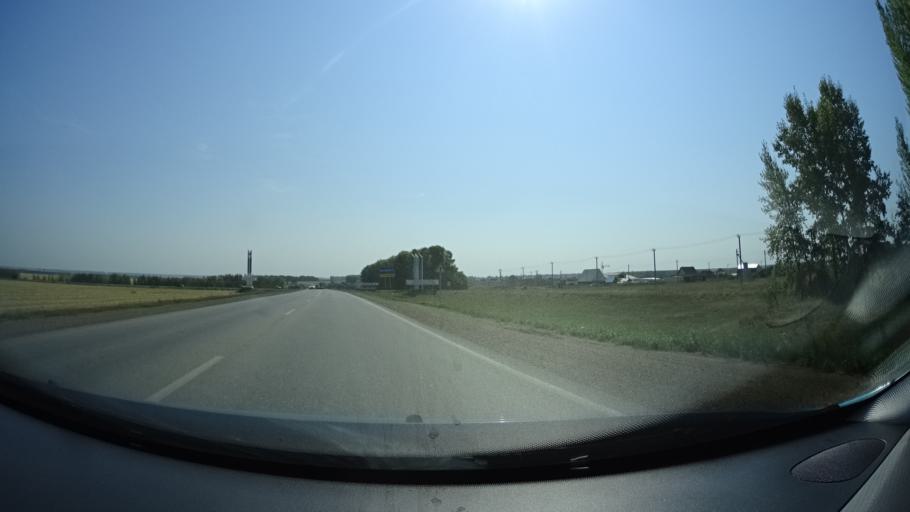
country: RU
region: Bashkortostan
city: Kabakovo
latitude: 54.4699
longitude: 55.9468
